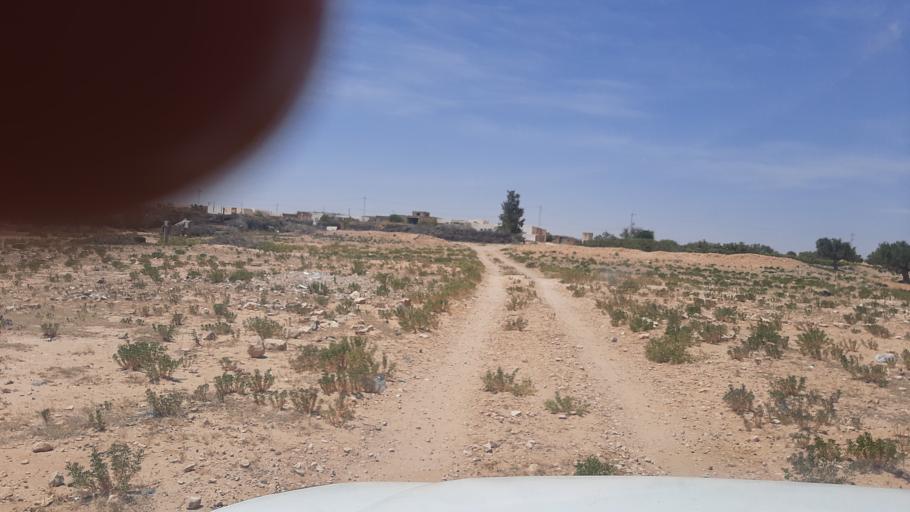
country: TN
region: Safaqis
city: Bi'r `Ali Bin Khalifah
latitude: 34.5649
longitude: 10.3460
